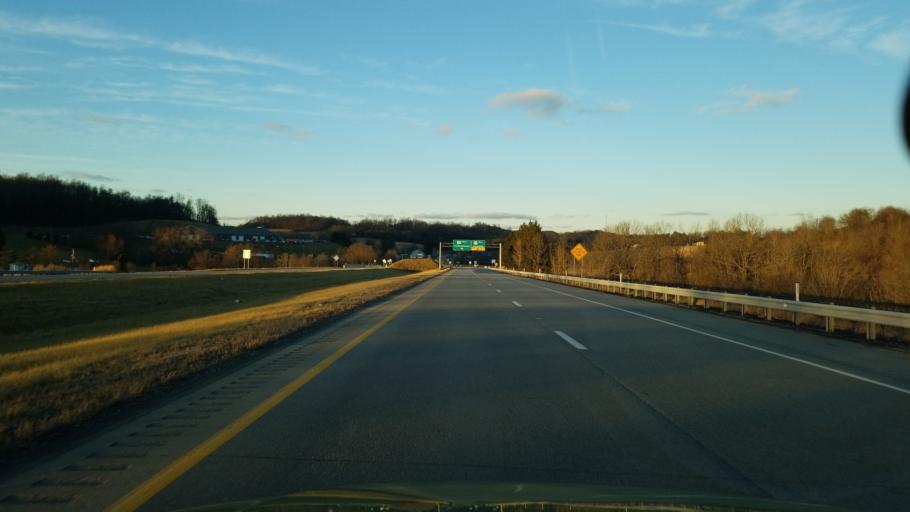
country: US
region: Pennsylvania
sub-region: Indiana County
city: Chevy Chase Heights
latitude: 40.6652
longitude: -79.1135
